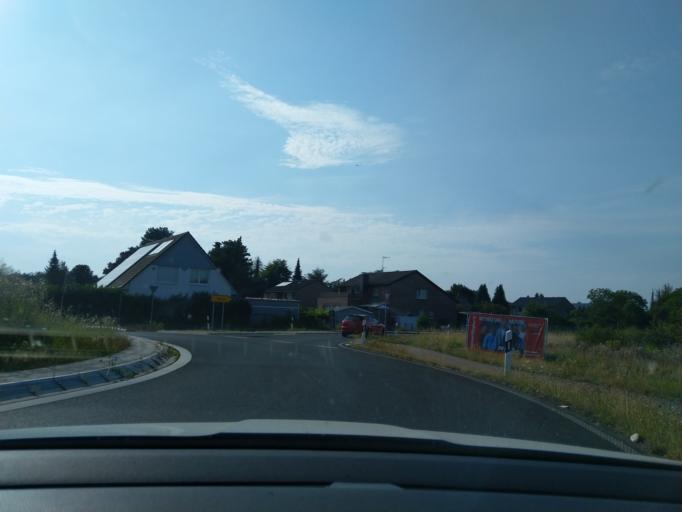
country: DE
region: North Rhine-Westphalia
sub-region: Regierungsbezirk Koln
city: Wassenberg
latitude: 51.1311
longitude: 6.1913
